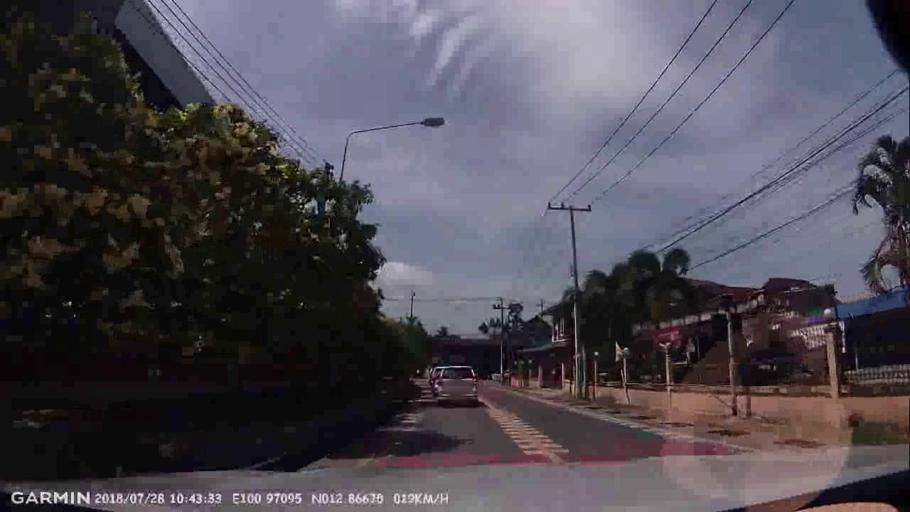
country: TH
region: Chon Buri
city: Phatthaya
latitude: 12.8667
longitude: 100.9709
